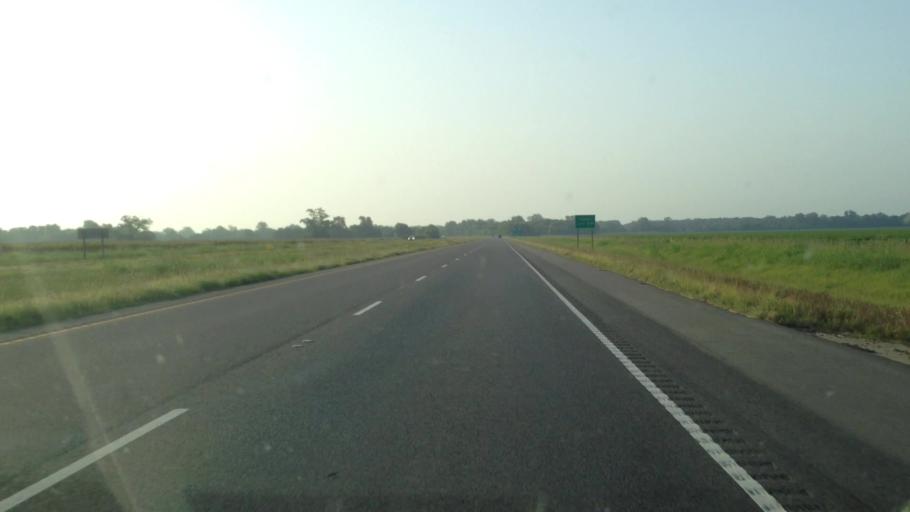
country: US
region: Louisiana
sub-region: Rapides Parish
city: Boyce
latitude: 31.3879
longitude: -92.6868
